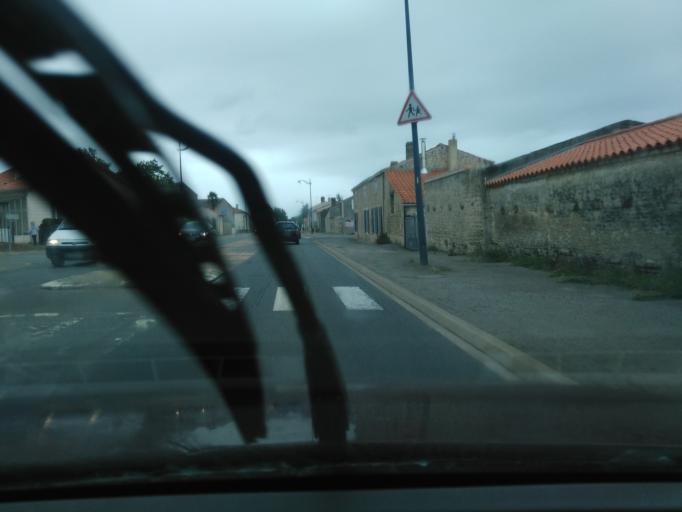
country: FR
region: Pays de la Loire
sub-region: Departement de la Vendee
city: Sainte-Gemme-la-Plaine
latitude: 46.4794
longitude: -1.1120
